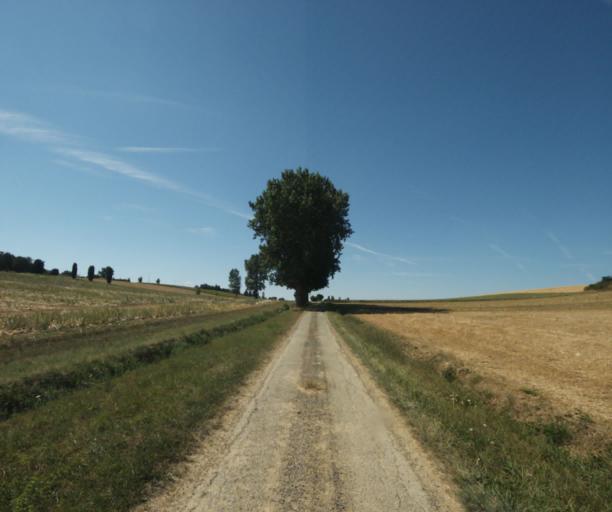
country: FR
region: Midi-Pyrenees
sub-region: Departement de la Haute-Garonne
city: Saint-Felix-Lauragais
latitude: 43.4999
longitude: 1.9278
